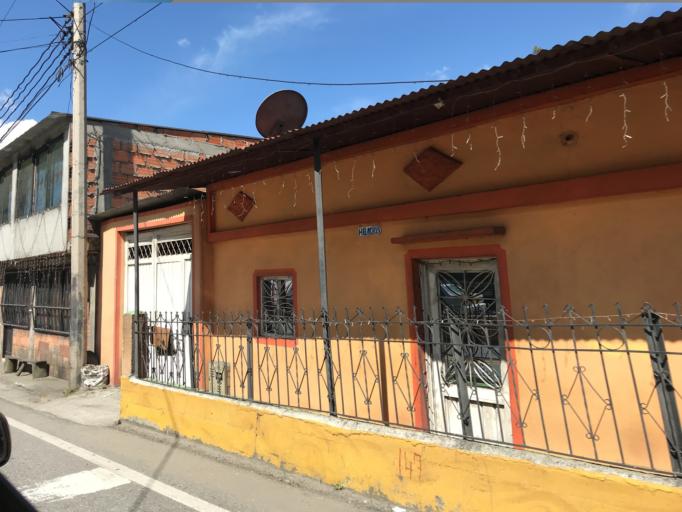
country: CO
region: Tolima
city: Cajamarca
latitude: 4.4370
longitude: -75.4368
